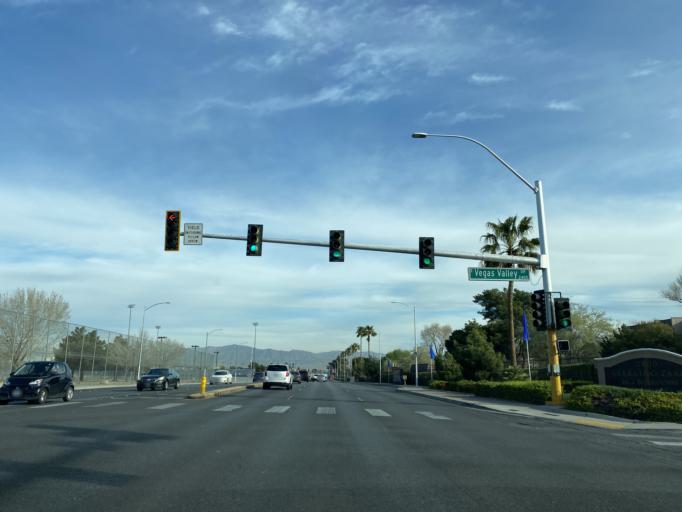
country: US
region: Nevada
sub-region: Clark County
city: Winchester
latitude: 36.1369
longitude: -115.1185
